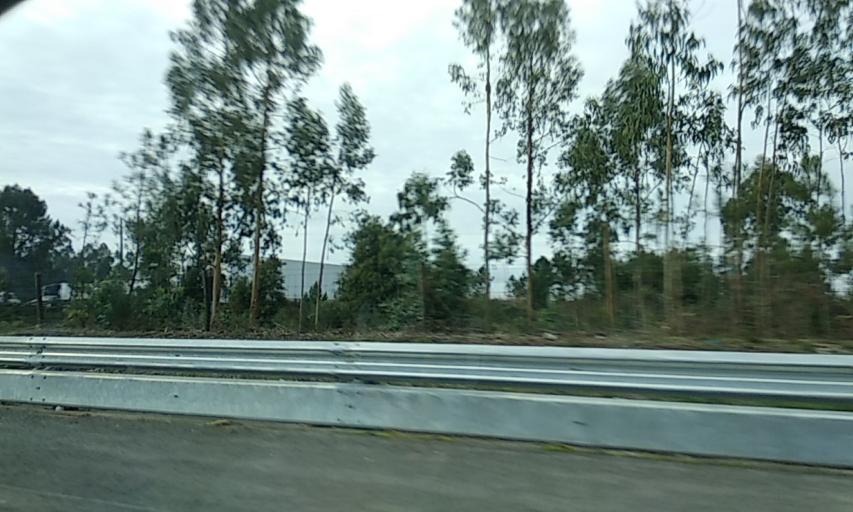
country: PT
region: Porto
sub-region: Santo Tirso
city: Santo Tirso
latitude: 41.3516
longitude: -8.5073
